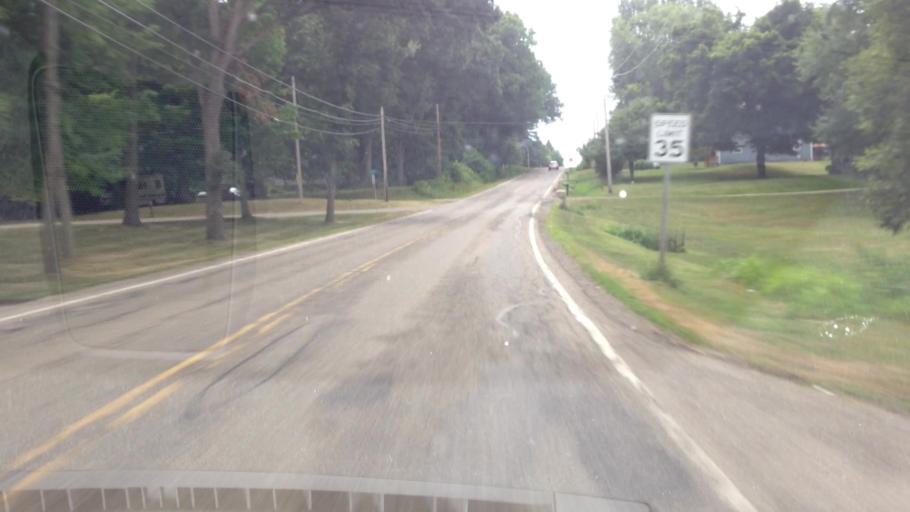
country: US
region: Ohio
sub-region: Summit County
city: Lakemore
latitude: 40.9861
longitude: -81.4489
